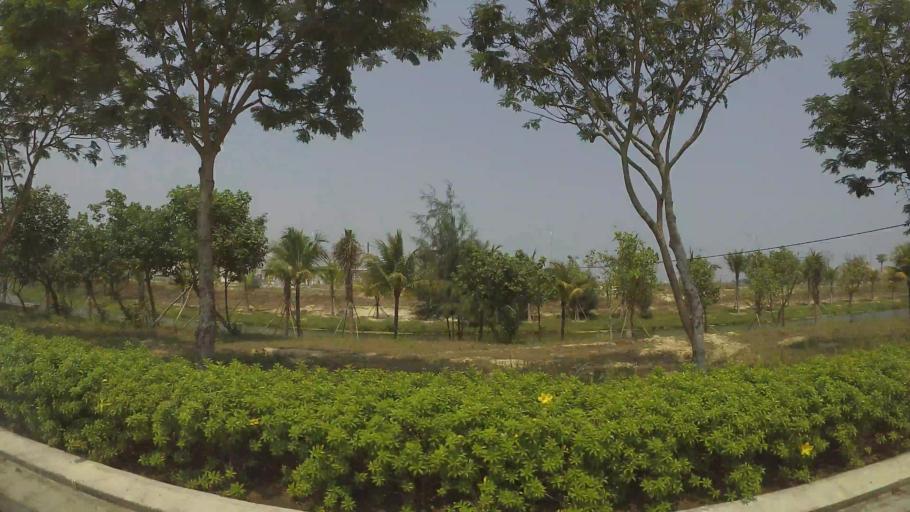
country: VN
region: Da Nang
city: Ngu Hanh Son
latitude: 15.9732
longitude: 108.2629
